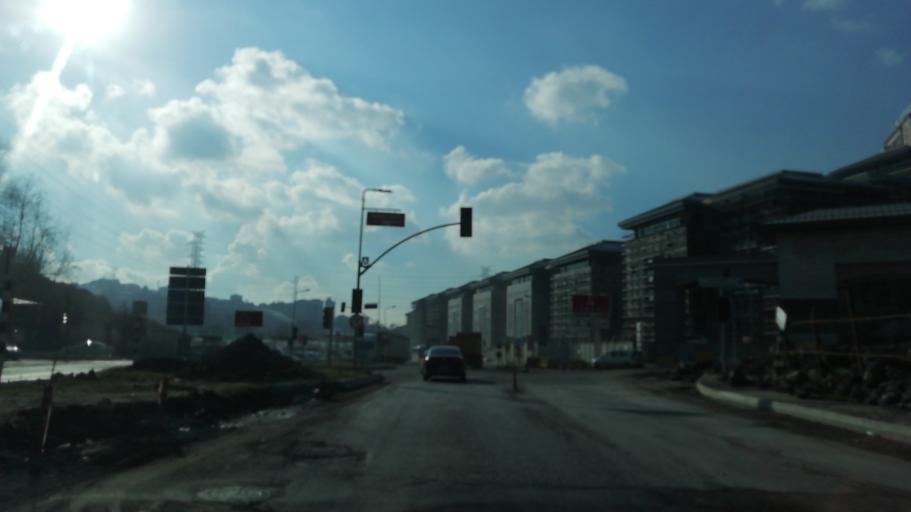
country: TR
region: Istanbul
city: Sisli
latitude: 41.0900
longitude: 28.9538
